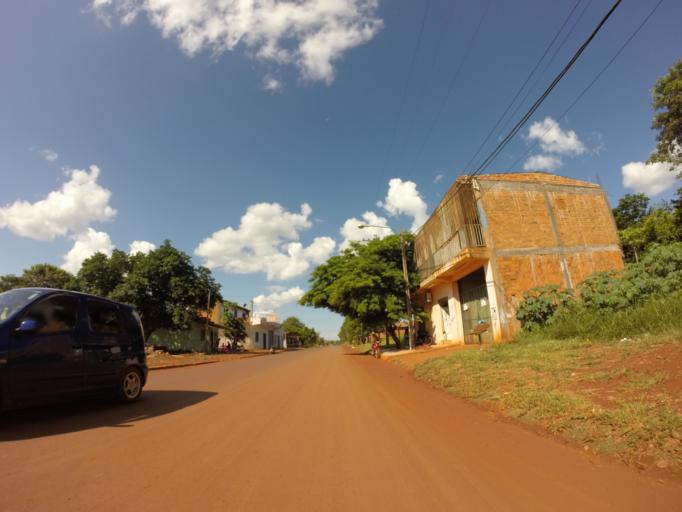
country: PY
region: Alto Parana
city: Ciudad del Este
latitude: -25.3756
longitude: -54.6578
